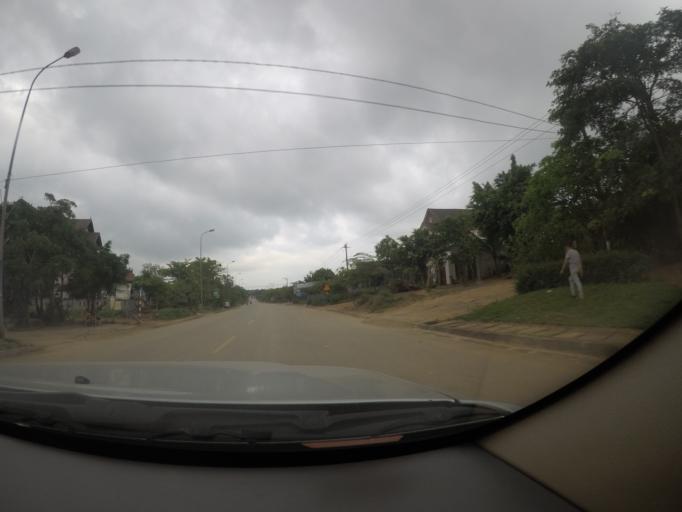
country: VN
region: Quang Tri
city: Ho Xa
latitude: 17.0186
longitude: 106.9062
